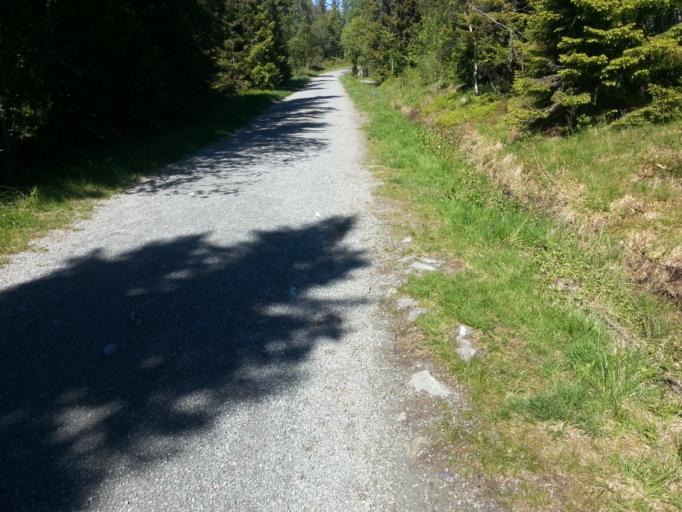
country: NO
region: Sor-Trondelag
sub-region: Trondheim
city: Trondheim
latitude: 63.4075
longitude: 10.2892
